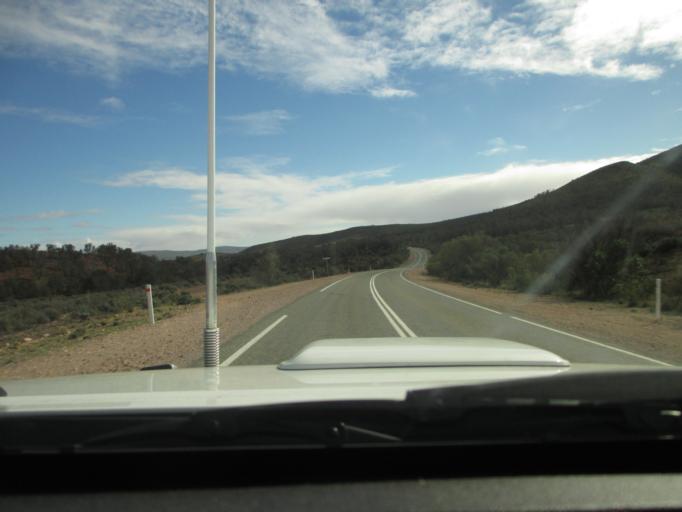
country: AU
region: South Australia
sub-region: Flinders Ranges
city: Quorn
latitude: -31.7905
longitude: 138.3540
